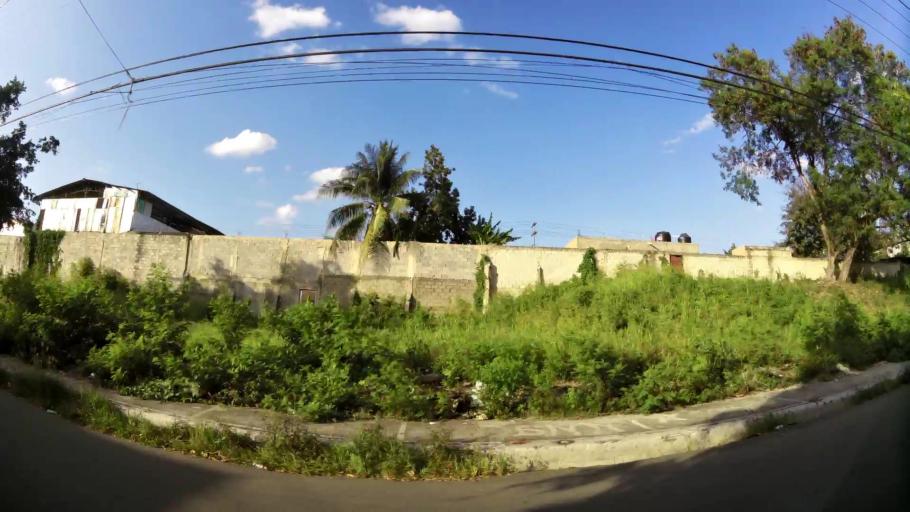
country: DO
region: Nacional
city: Ensanche Luperon
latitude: 18.5465
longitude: -69.9044
